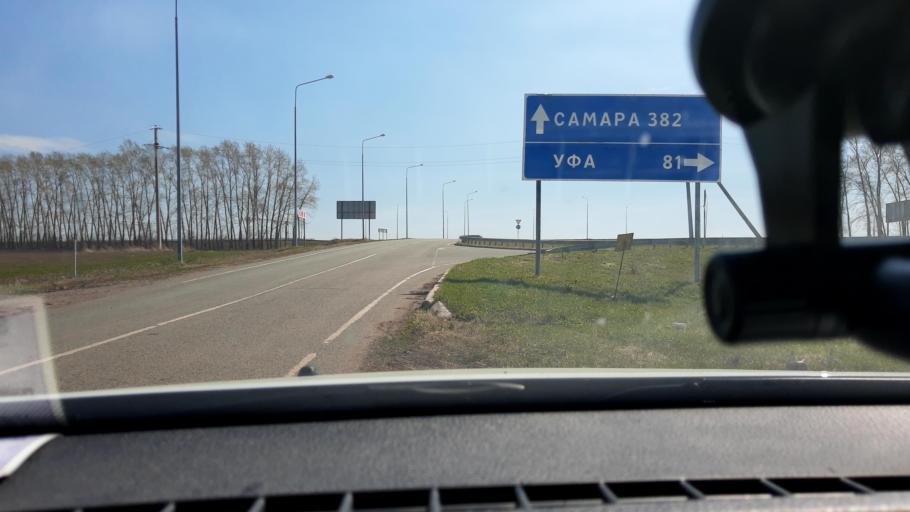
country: RU
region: Bashkortostan
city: Alekseyevka
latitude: 54.7265
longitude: 54.9242
